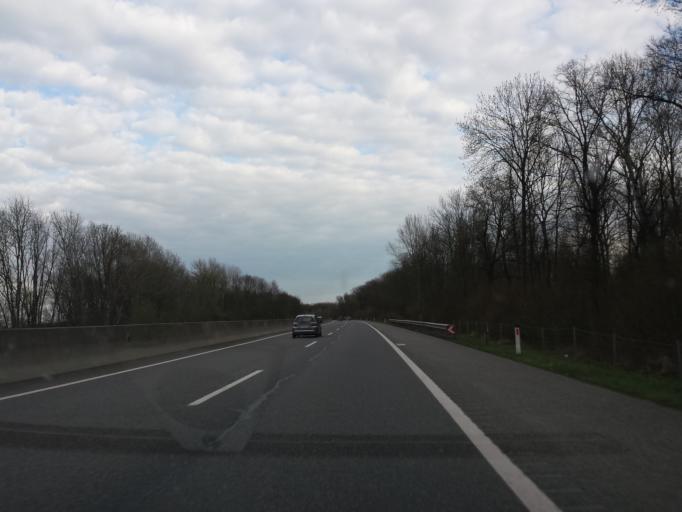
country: AT
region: Lower Austria
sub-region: Politischer Bezirk Tulln
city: Kirchberg am Wagram
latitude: 48.3721
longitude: 15.9362
